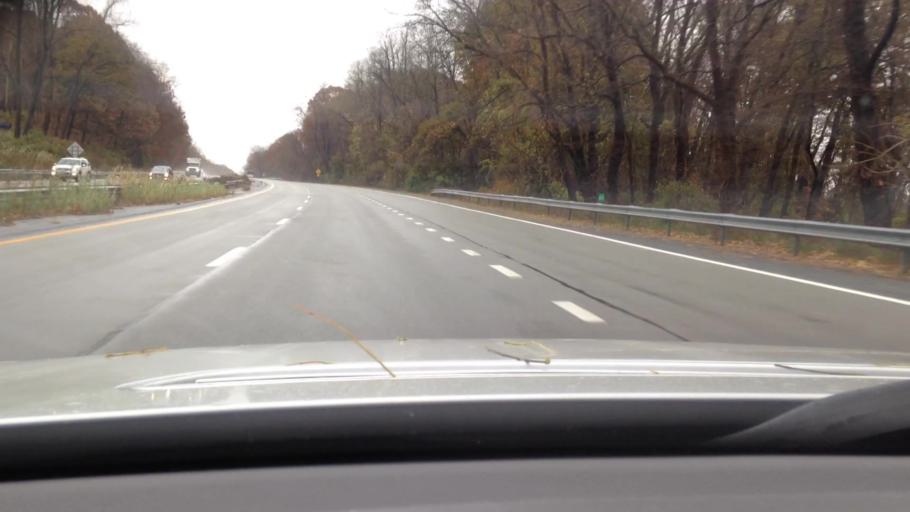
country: US
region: New York
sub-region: Westchester County
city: Buchanan
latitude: 41.2665
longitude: -73.9341
